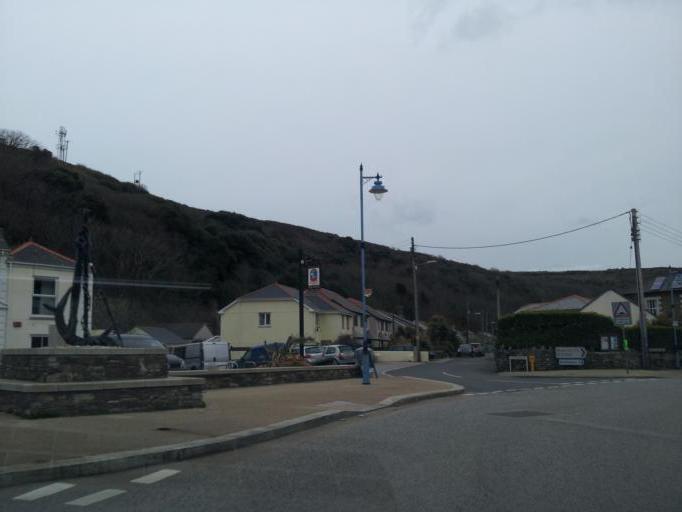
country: GB
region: England
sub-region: Cornwall
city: Camborne
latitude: 50.2613
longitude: -5.2884
